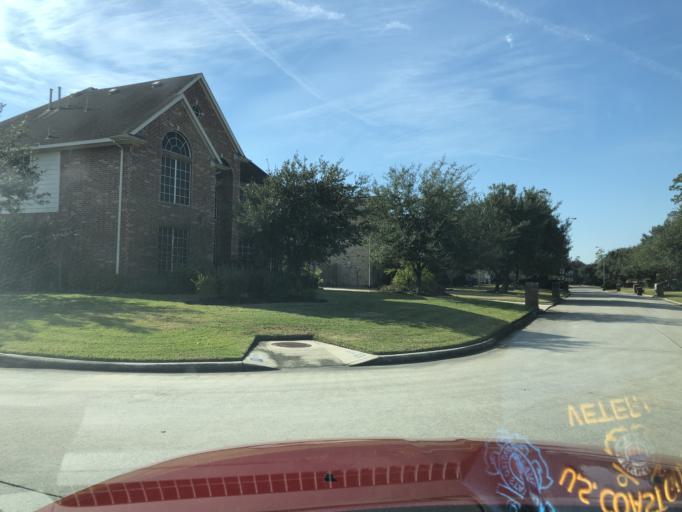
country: US
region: Texas
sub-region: Harris County
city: Tomball
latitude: 30.0283
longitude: -95.5579
